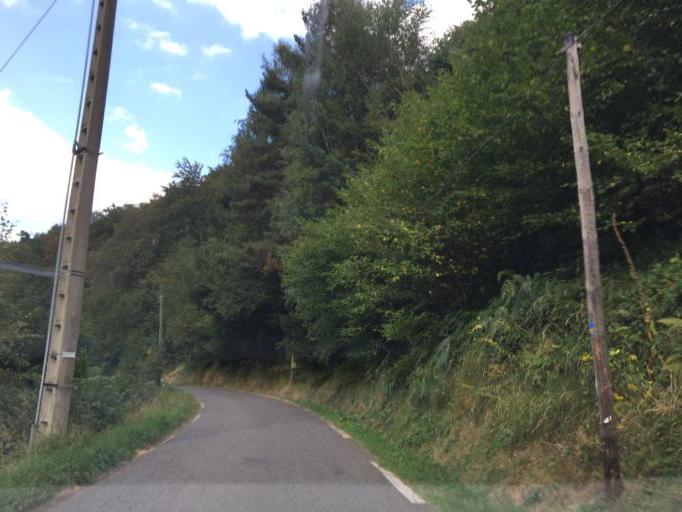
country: FR
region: Rhone-Alpes
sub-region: Departement de la Loire
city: Saint-Jean-Bonnefonds
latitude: 45.3976
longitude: 4.4472
